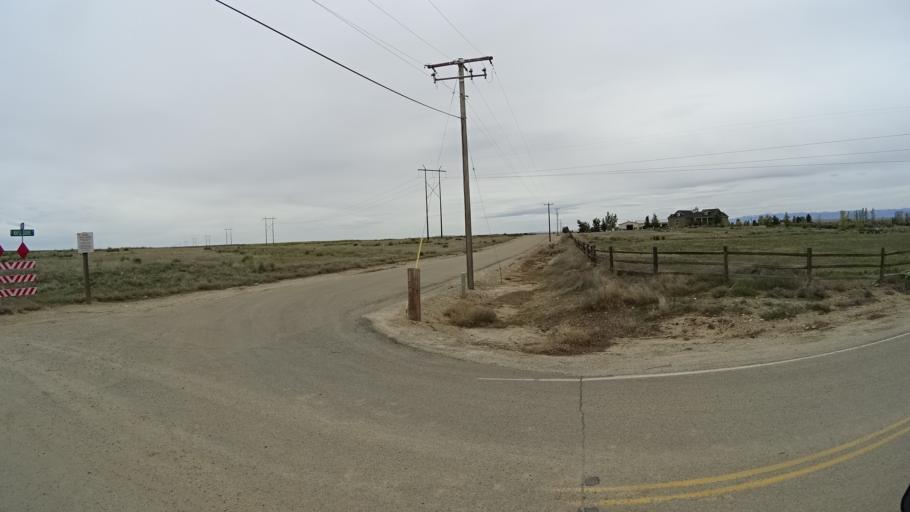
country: US
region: Idaho
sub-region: Ada County
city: Kuna
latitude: 43.4884
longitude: -116.2948
